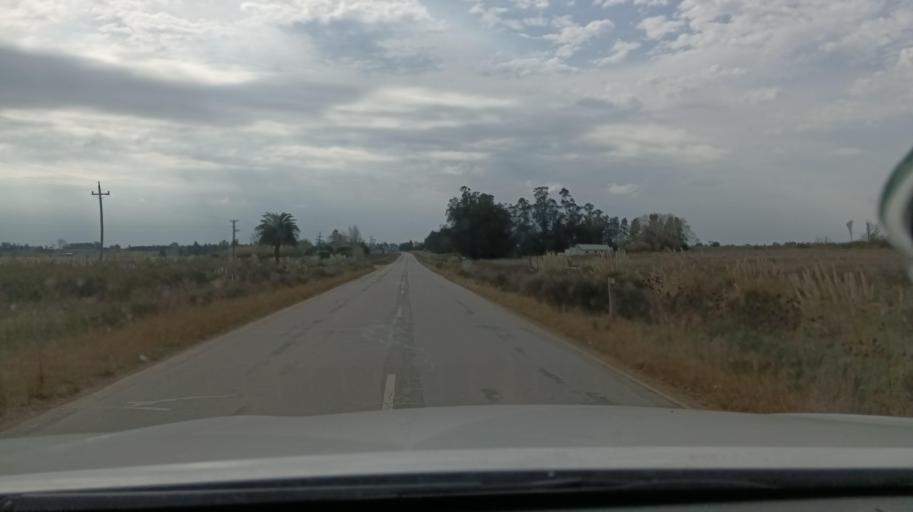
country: UY
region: Canelones
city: Sauce
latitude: -34.6490
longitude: -56.1067
